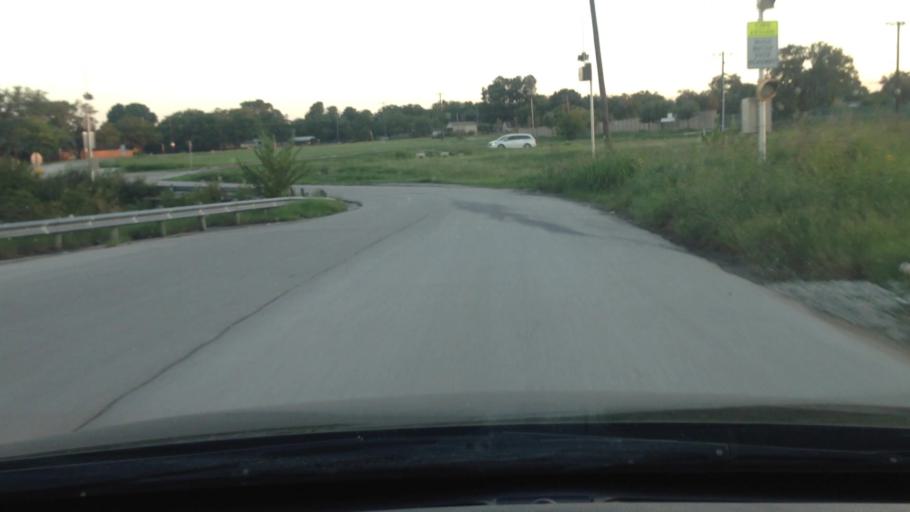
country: US
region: Texas
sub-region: Tarrant County
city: White Settlement
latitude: 32.7790
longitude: -97.4674
